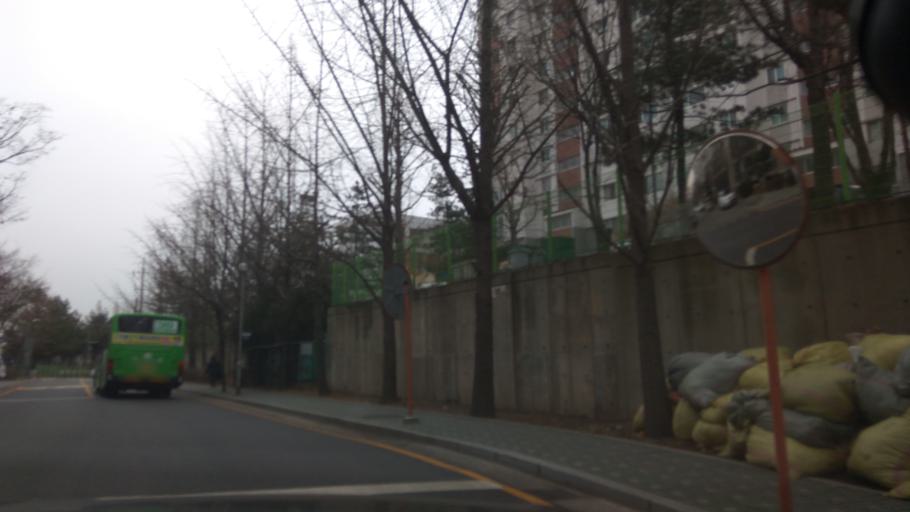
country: KR
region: Incheon
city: Incheon
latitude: 37.4947
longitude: 126.7076
